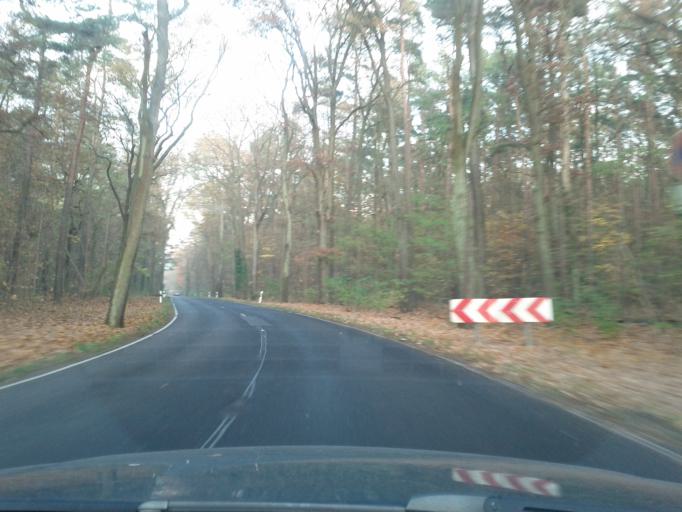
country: DE
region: Berlin
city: Rahnsdorf
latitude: 52.4481
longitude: 13.6874
